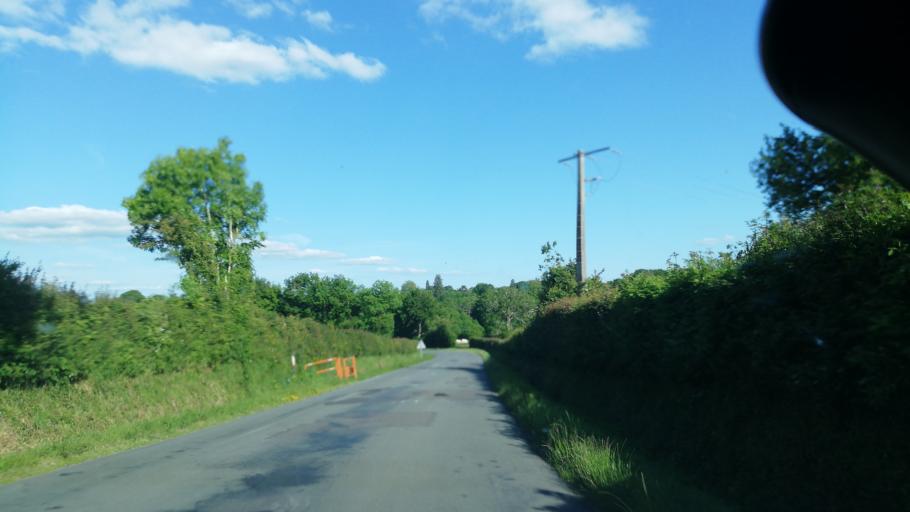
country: FR
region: Poitou-Charentes
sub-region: Departement des Deux-Sevres
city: La Chapelle-Saint-Laurent
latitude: 46.7484
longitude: -0.4869
